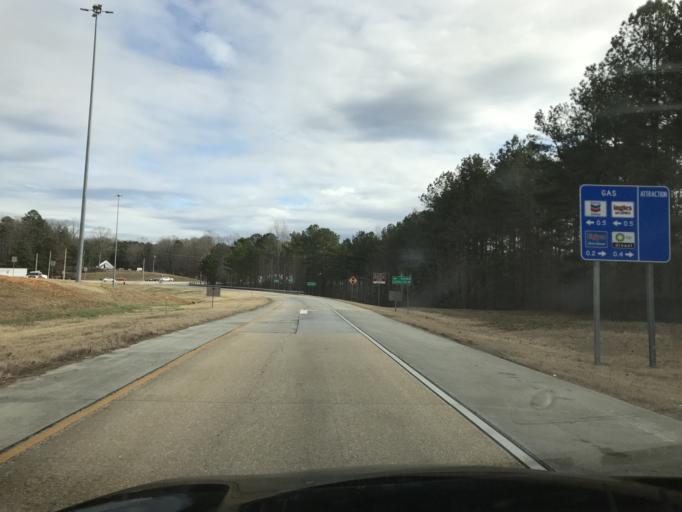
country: US
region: Georgia
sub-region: Haralson County
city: Bremen
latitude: 33.6842
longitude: -85.1538
